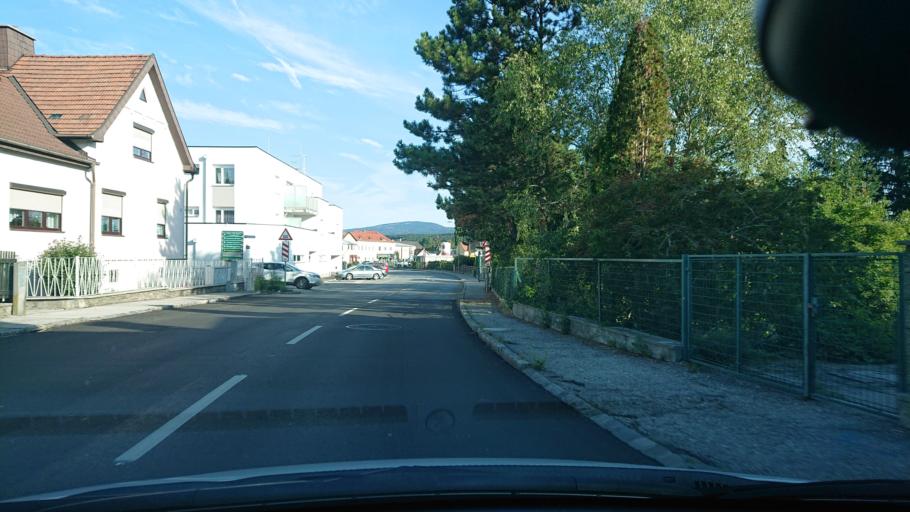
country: AT
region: Lower Austria
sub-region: Politischer Bezirk Baden
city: Hirtenberg
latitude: 47.9197
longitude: 16.1862
